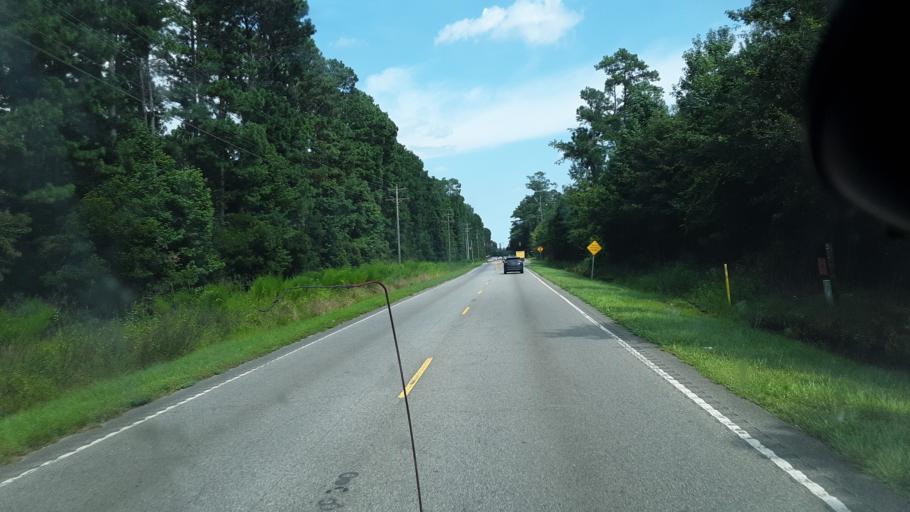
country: US
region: South Carolina
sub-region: Horry County
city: Red Hill
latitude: 33.8222
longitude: -78.9176
